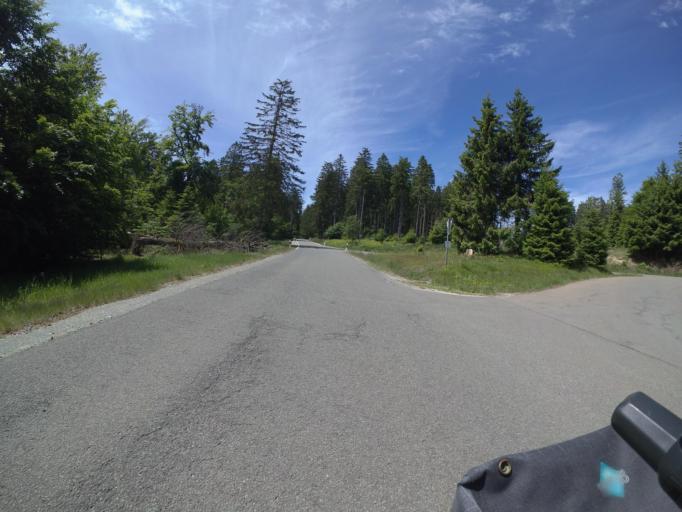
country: DE
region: Rheinland-Pfalz
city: Borfink
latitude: 49.7311
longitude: 7.0983
